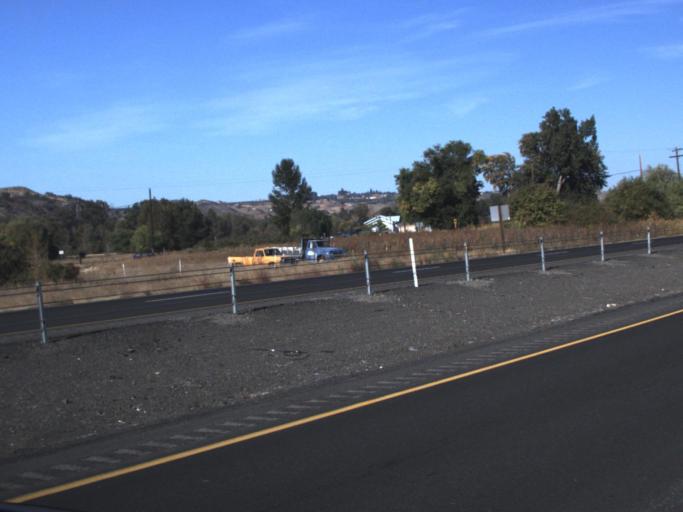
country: US
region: Washington
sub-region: Yakima County
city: Gleed
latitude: 46.6370
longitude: -120.5921
